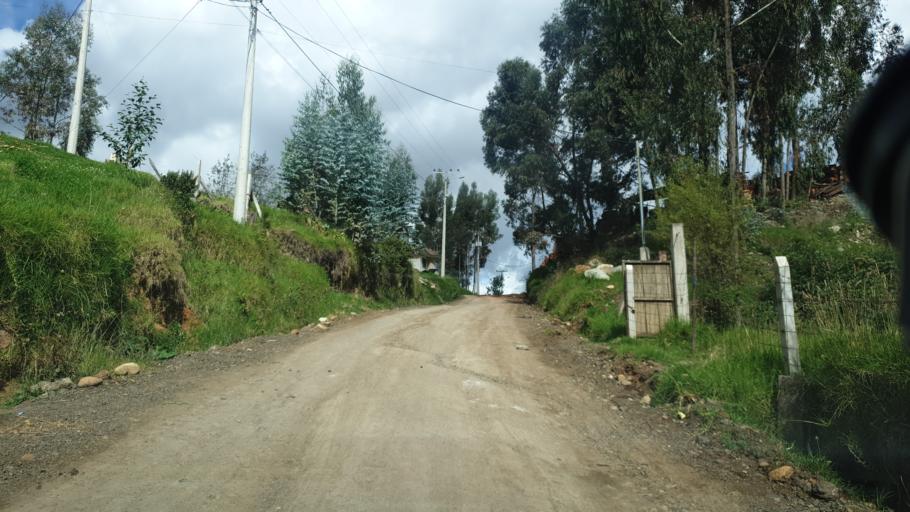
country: EC
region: Azuay
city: Cuenca
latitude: -2.8590
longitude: -79.0417
